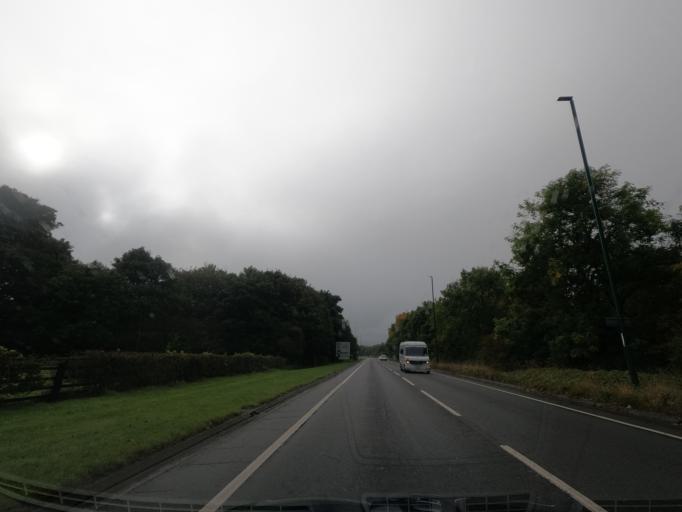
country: GB
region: England
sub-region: Redcar and Cleveland
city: Redcar
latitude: 54.5911
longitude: -1.0847
